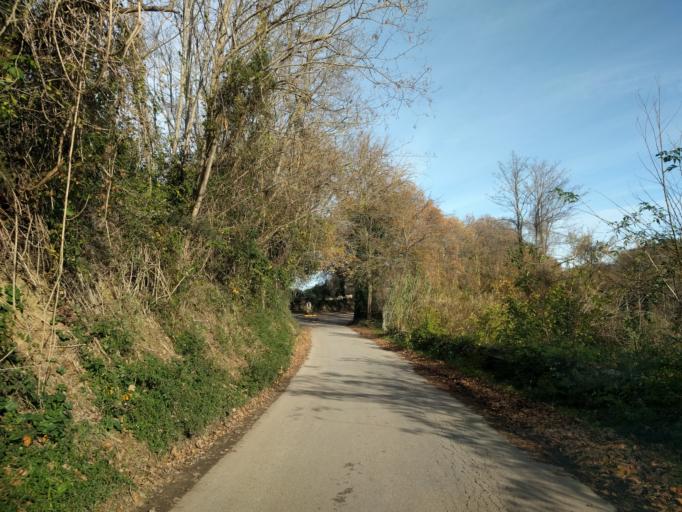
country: IT
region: The Marches
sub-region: Provincia di Pesaro e Urbino
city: Cuccurano
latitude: 43.8134
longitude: 12.9665
